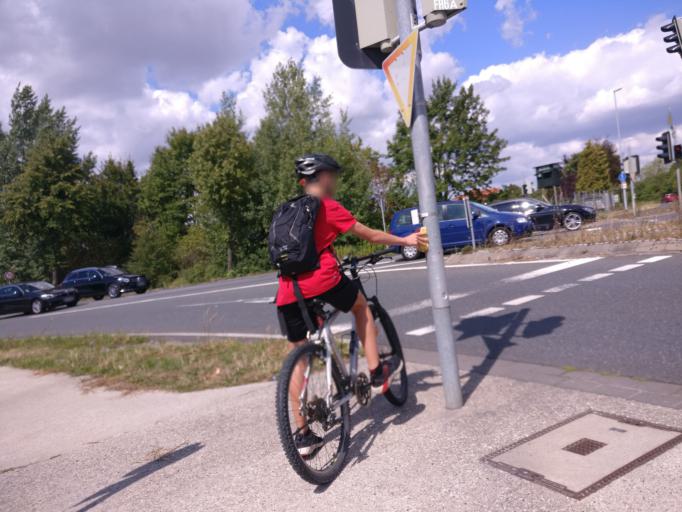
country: DE
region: Lower Saxony
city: Hildesheim
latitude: 52.1612
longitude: 9.9979
